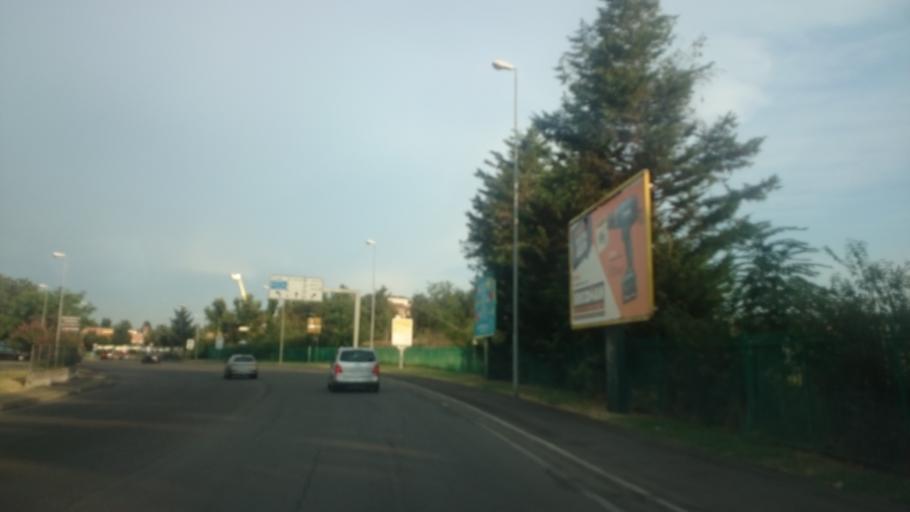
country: IT
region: Emilia-Romagna
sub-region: Provincia di Reggio Emilia
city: Reggio nell'Emilia
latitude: 44.7086
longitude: 10.6373
